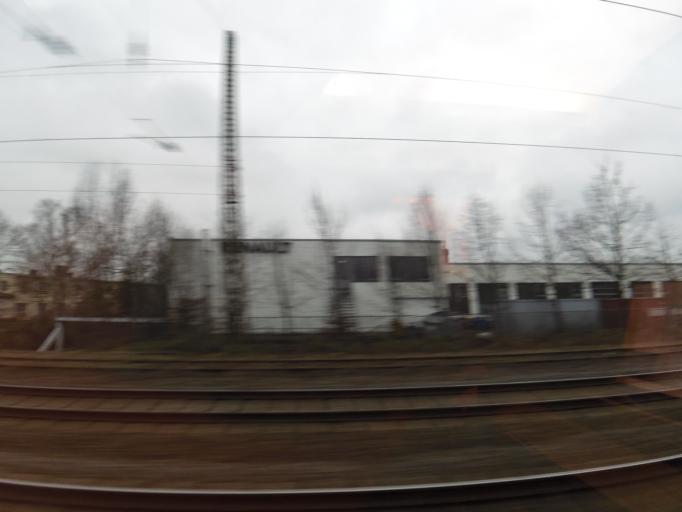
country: DE
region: Saxony
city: Leipzig
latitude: 51.3770
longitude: 12.3967
